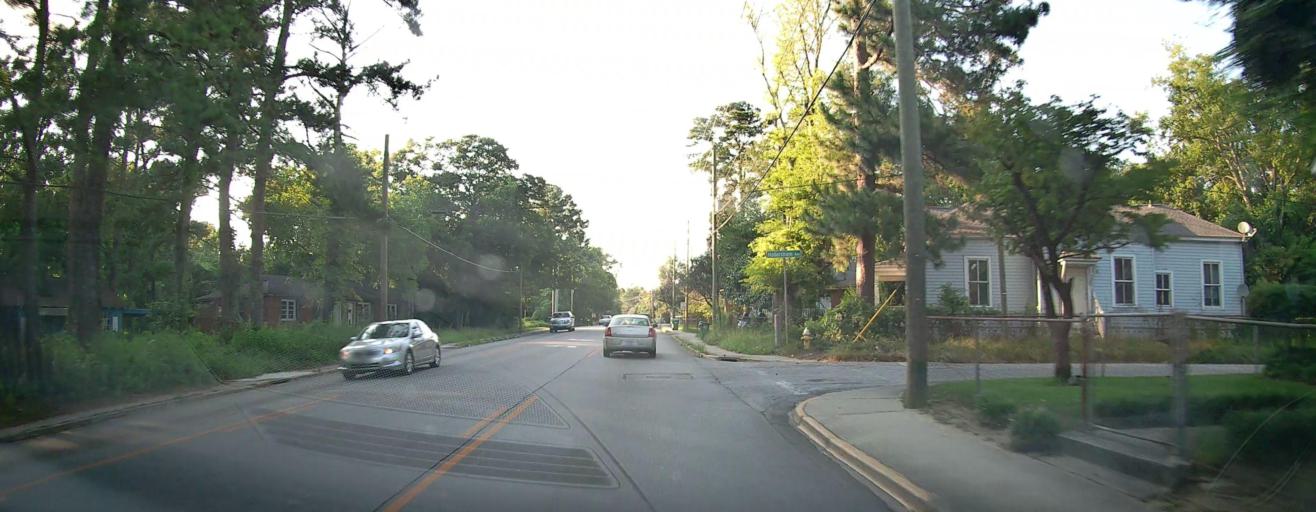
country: US
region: Georgia
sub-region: Bibb County
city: Macon
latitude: 32.8436
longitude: -83.6878
